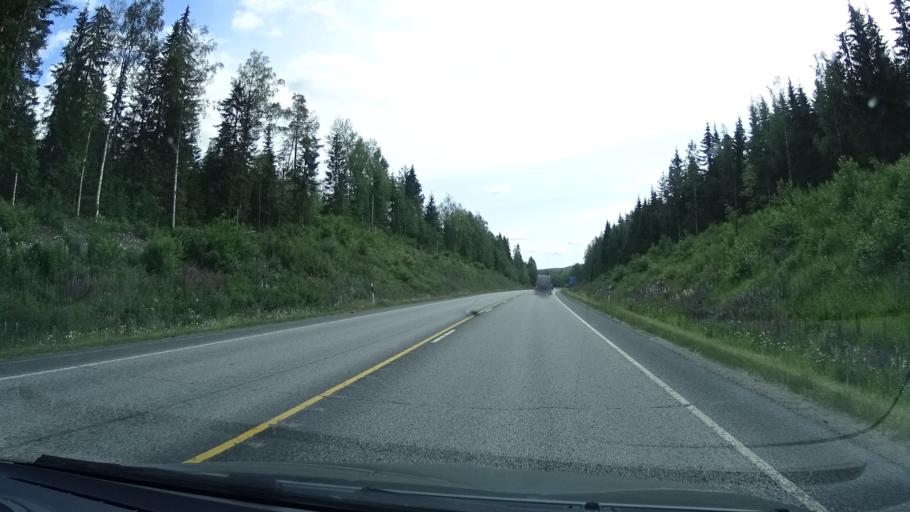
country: FI
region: Central Finland
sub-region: Jyvaeskylae
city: Jyvaeskylae
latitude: 62.2639
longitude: 25.5849
